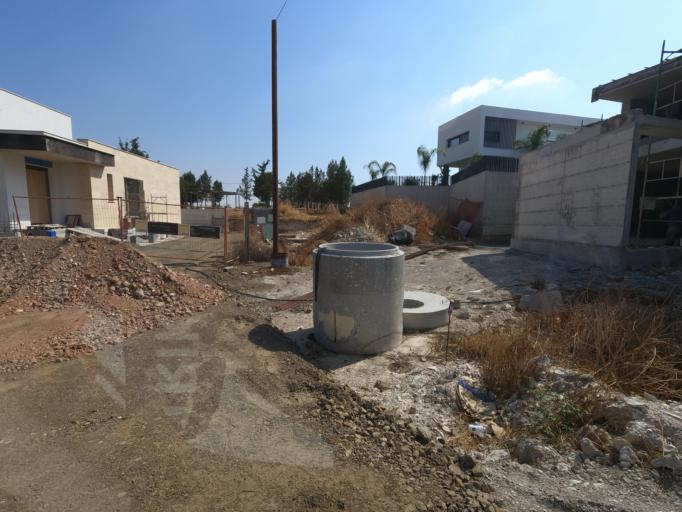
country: CY
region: Lefkosia
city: Lympia
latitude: 34.9959
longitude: 33.4722
